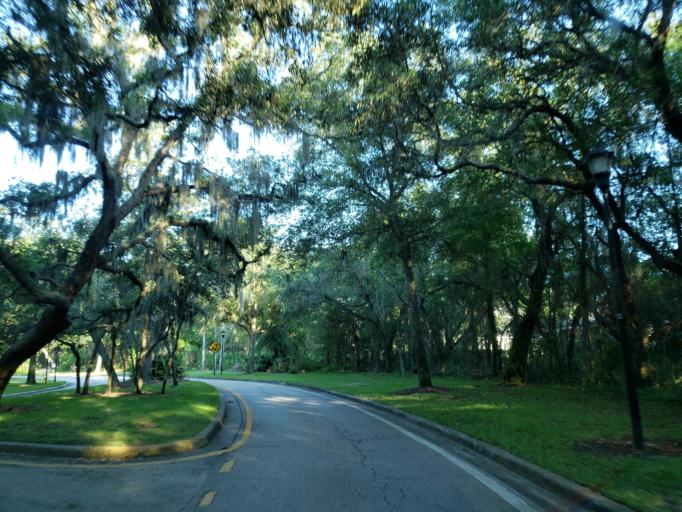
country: US
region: Florida
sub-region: Hillsborough County
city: Boyette
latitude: 27.8378
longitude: -82.2339
